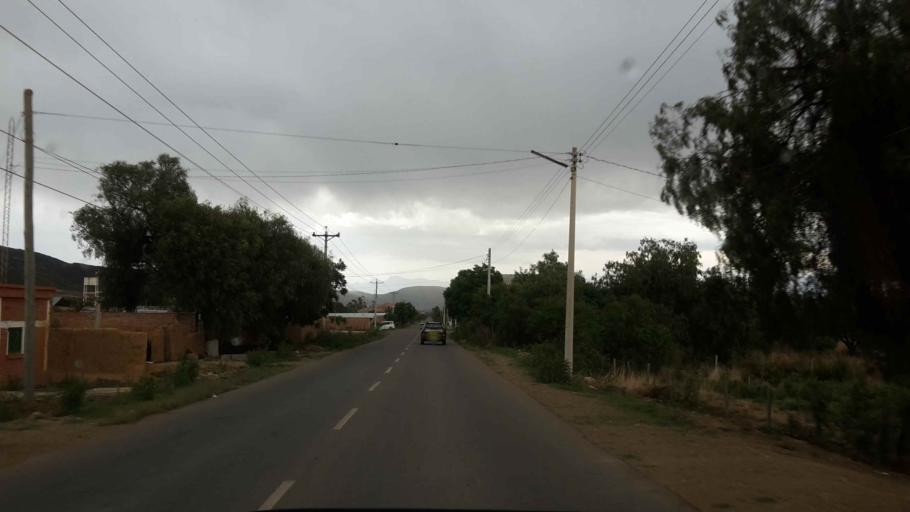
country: BO
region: Cochabamba
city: Tarata
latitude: -17.5918
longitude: -66.0447
